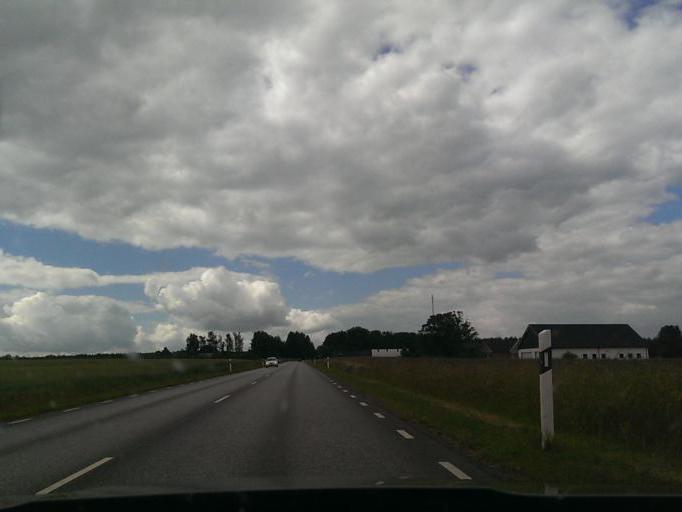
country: SE
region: Skane
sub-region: Eslovs Kommun
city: Stehag
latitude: 55.9201
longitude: 13.3698
